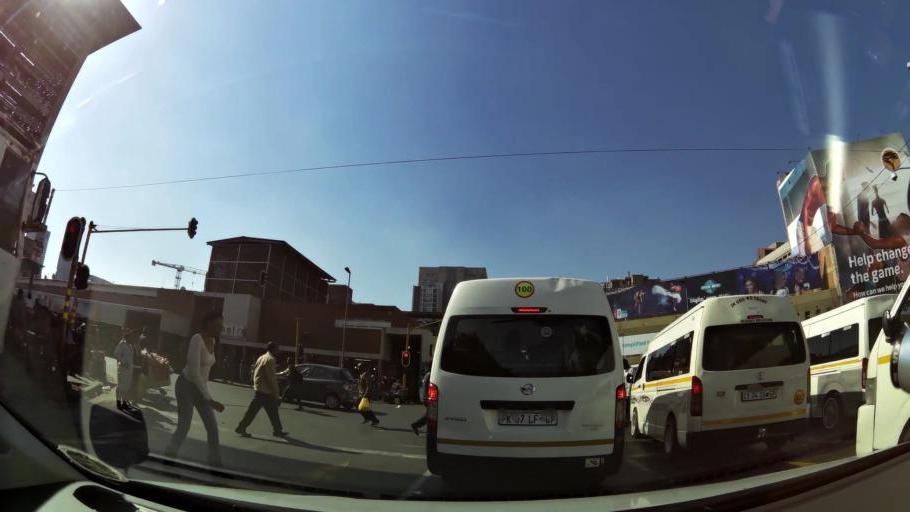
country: ZA
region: Gauteng
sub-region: City of Johannesburg Metropolitan Municipality
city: Johannesburg
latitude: -26.2013
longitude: 28.0372
